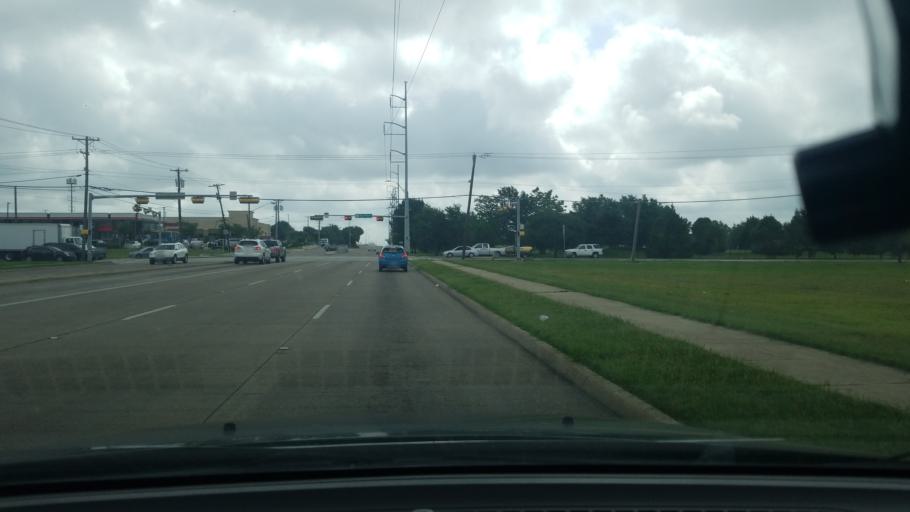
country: US
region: Texas
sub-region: Dallas County
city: Balch Springs
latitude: 32.7924
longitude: -96.6859
